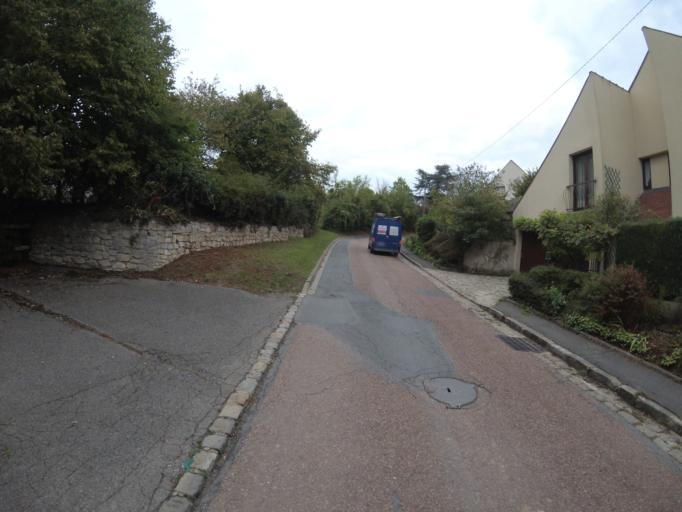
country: FR
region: Ile-de-France
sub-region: Departement de Seine-et-Marne
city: Gouvernes
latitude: 48.8619
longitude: 2.6910
